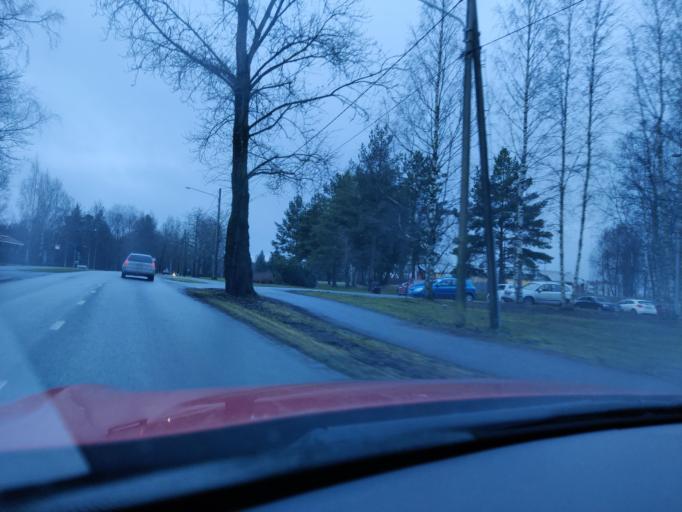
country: FI
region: Pirkanmaa
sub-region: Tampere
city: Nokia
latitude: 61.4844
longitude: 23.5299
